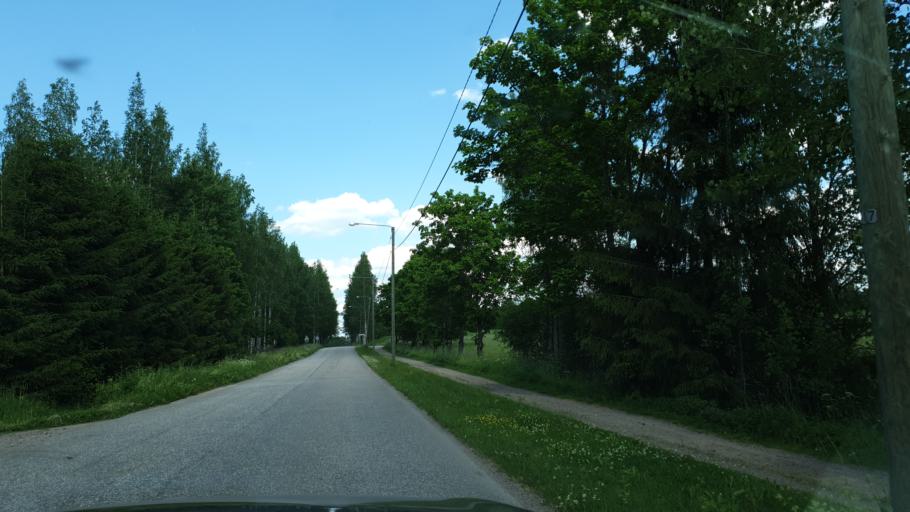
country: FI
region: Uusimaa
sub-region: Helsinki
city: Vihti
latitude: 60.3784
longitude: 24.5107
